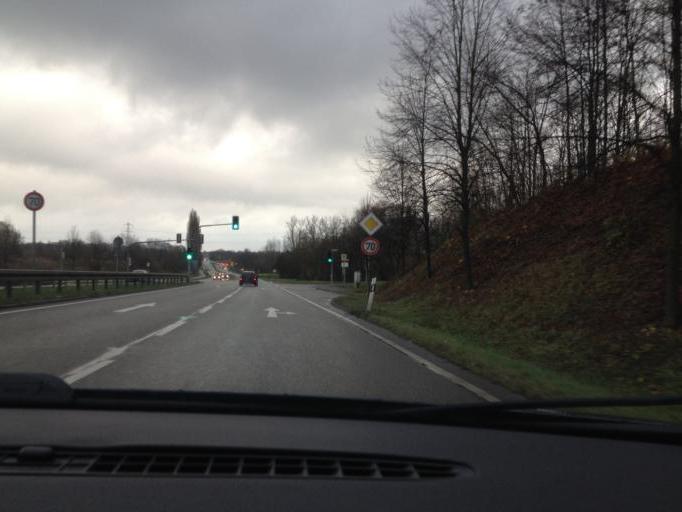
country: DE
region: Baden-Wuerttemberg
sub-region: Regierungsbezirk Stuttgart
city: Asperg
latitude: 48.9182
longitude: 9.1593
